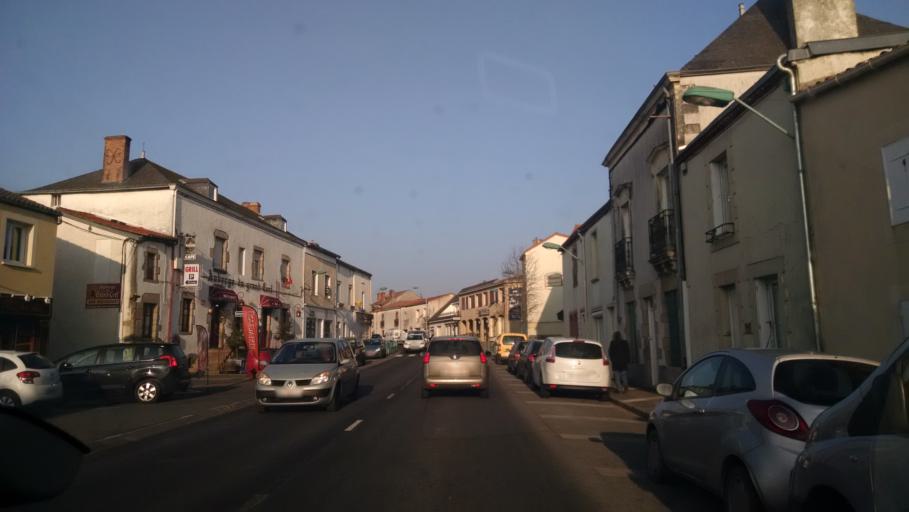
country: FR
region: Pays de la Loire
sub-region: Departement de la Loire-Atlantique
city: Aigrefeuille-sur-Maine
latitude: 47.0762
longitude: -1.3991
